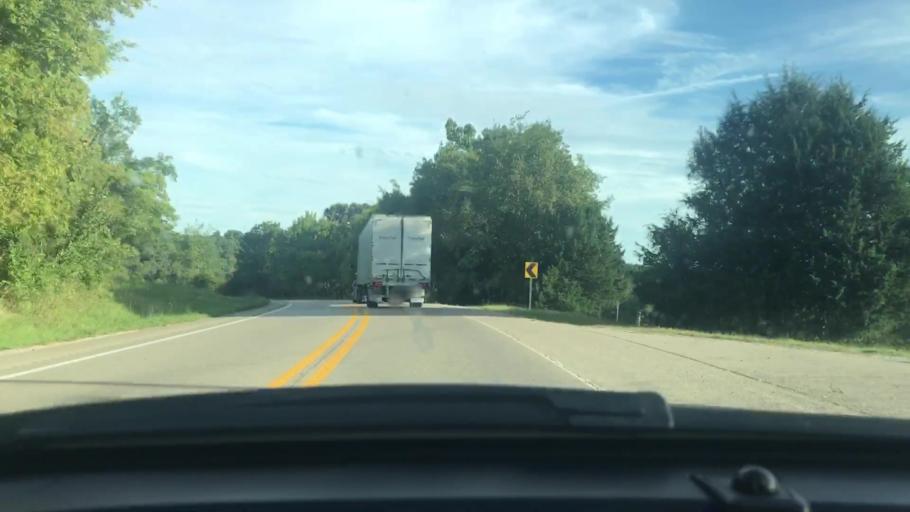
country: US
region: Arkansas
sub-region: Randolph County
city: Pocahontas
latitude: 36.2143
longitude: -91.2146
